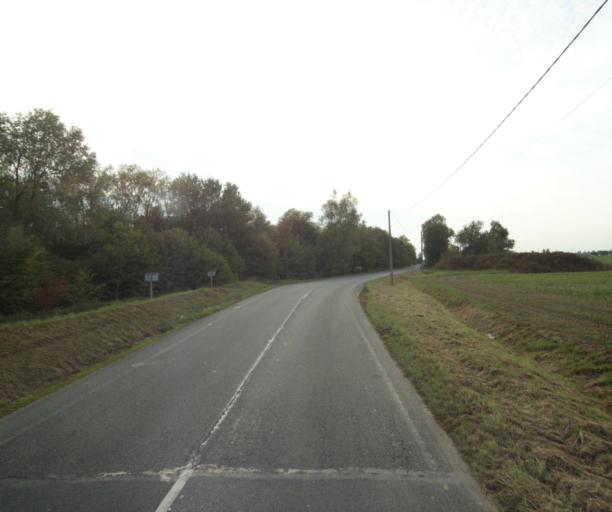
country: FR
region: Nord-Pas-de-Calais
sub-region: Departement du Nord
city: Avelin
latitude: 50.5432
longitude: 3.0668
